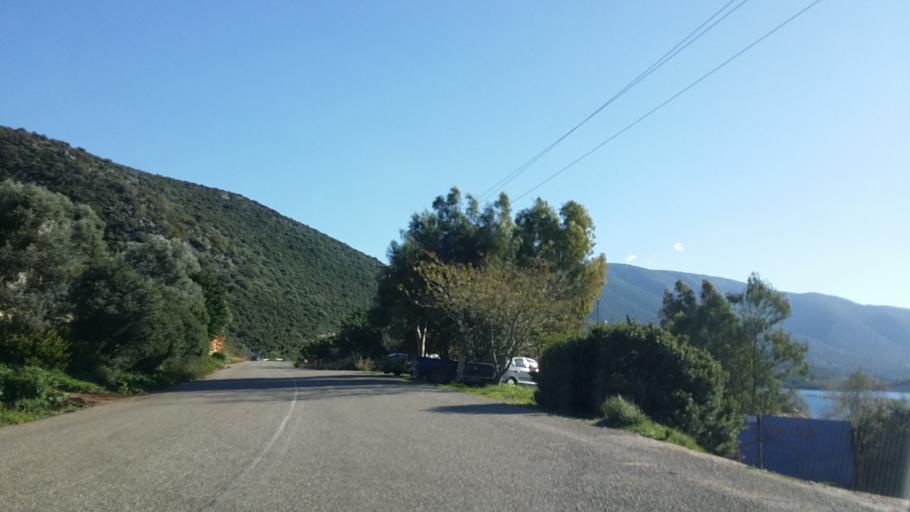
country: GR
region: West Greece
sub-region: Nomos Aitolias kai Akarnanias
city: Archontochorion
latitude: 38.6150
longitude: 21.0152
